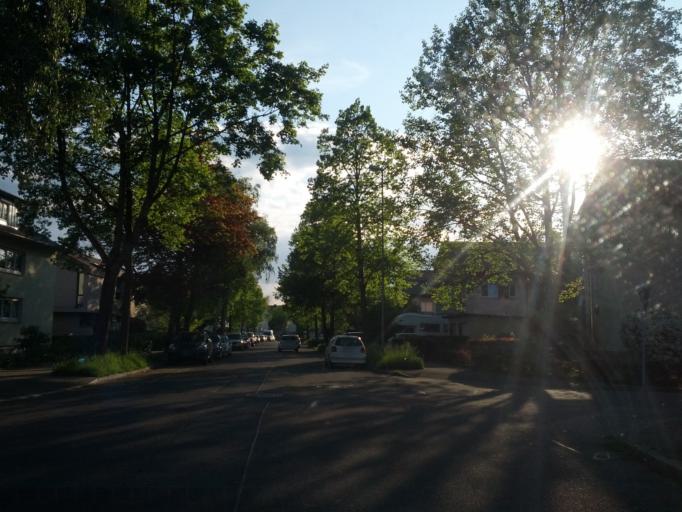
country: DE
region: Baden-Wuerttemberg
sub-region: Freiburg Region
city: Emmendingen
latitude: 48.1035
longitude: 7.8638
